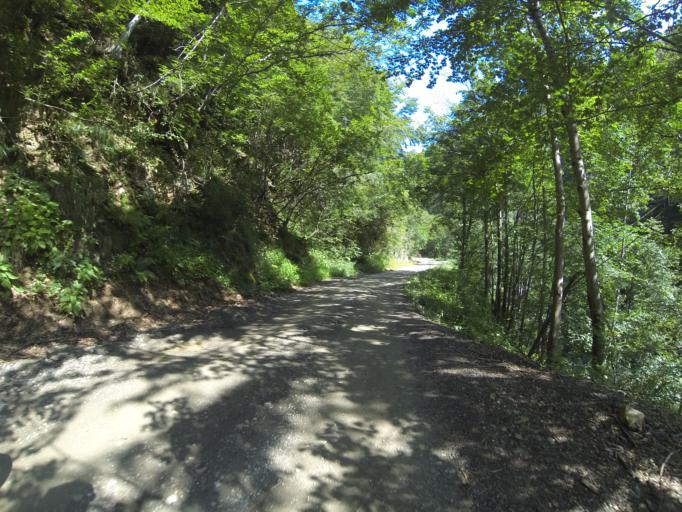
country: RO
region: Valcea
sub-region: Comuna Costesti
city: Bistrita
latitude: 45.2471
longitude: 23.9943
